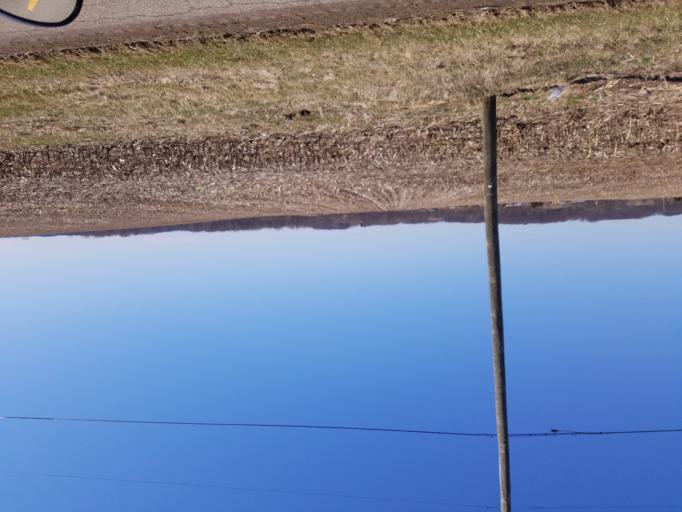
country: US
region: Ohio
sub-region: Knox County
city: Fredericktown
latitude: 40.4669
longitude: -82.5415
